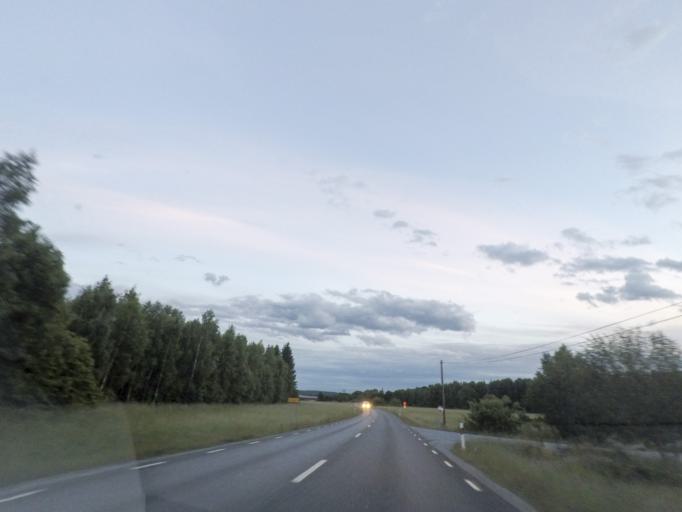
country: SE
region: Uppsala
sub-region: Habo Kommun
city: Balsta
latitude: 59.6501
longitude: 17.5400
